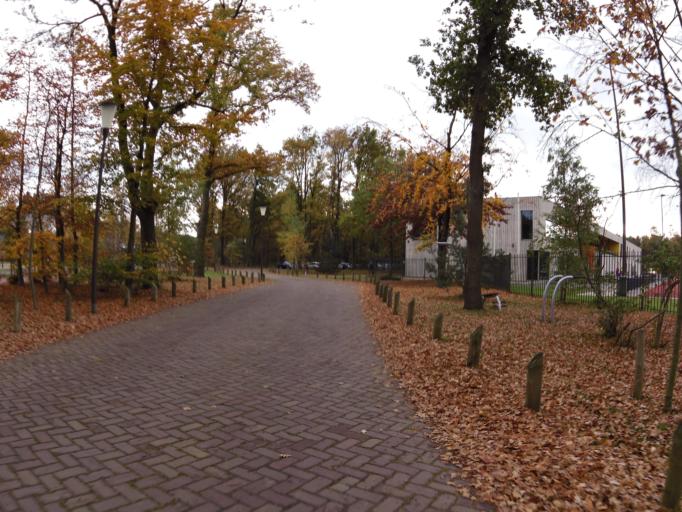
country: NL
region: North Brabant
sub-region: Gemeente Vught
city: Vught
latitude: 51.6659
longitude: 5.2805
